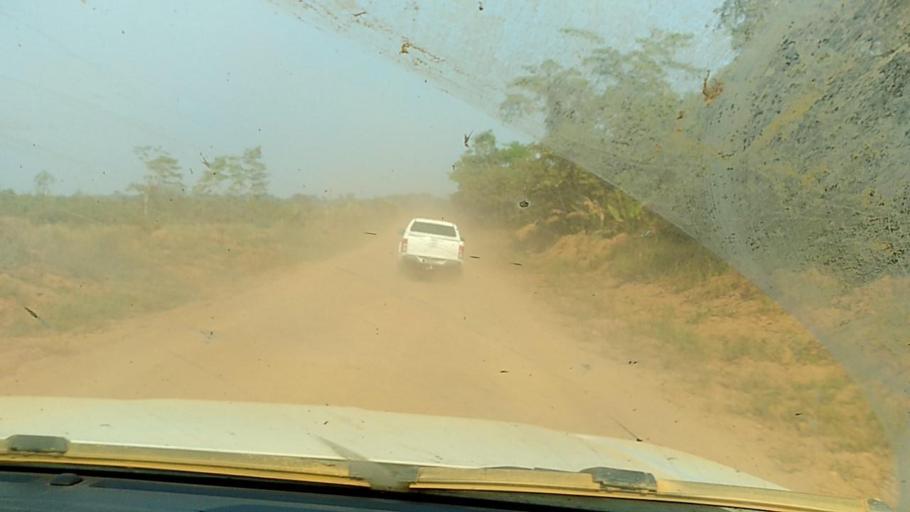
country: BR
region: Rondonia
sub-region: Porto Velho
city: Porto Velho
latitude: -8.7610
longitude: -64.0658
